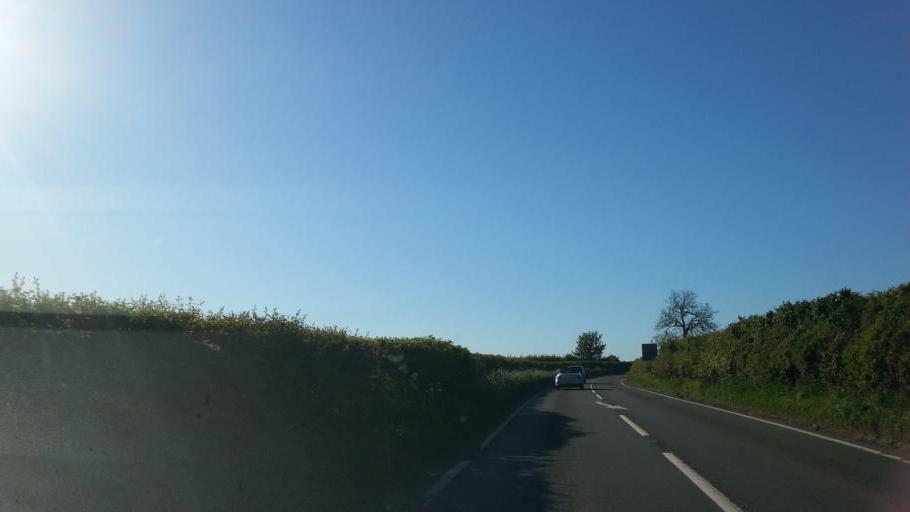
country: GB
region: England
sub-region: Somerset
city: Evercreech
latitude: 51.1410
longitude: -2.5184
